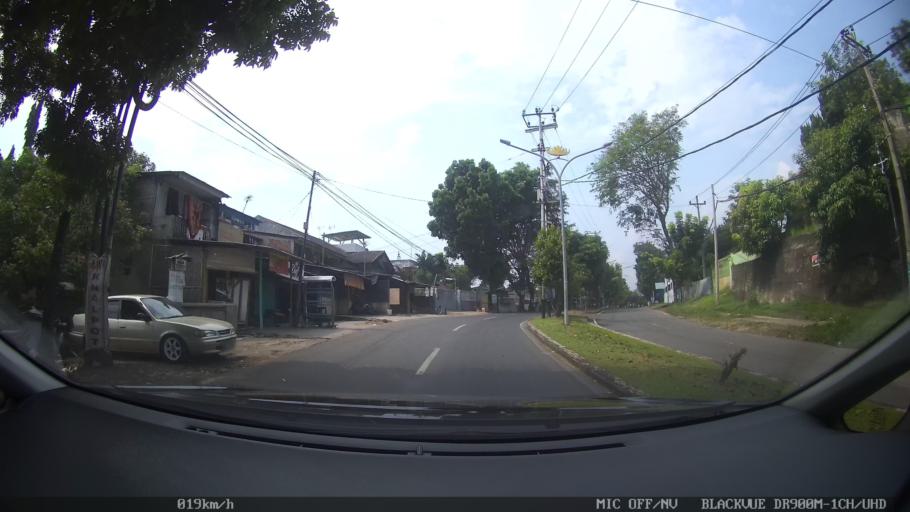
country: ID
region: Lampung
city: Bandarlampung
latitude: -5.4222
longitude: 105.2481
